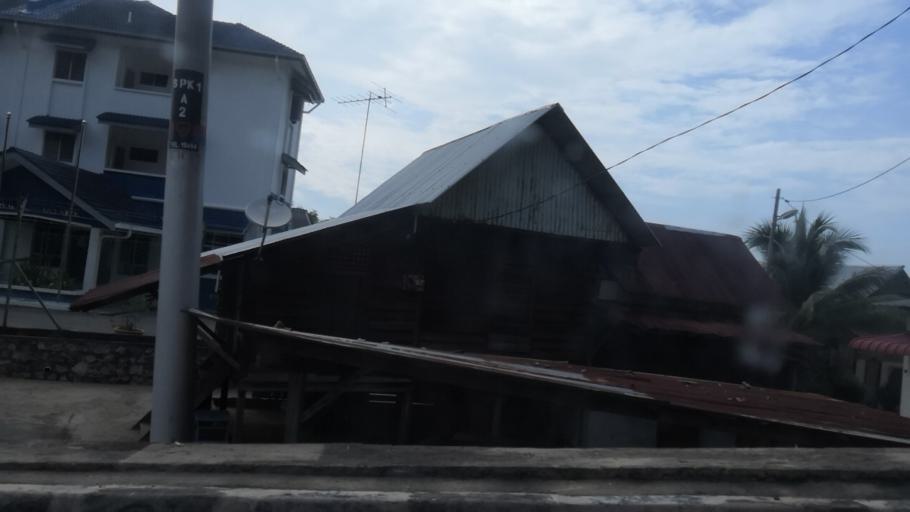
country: MY
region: Perak
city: Lumut
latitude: 4.2251
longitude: 100.5744
